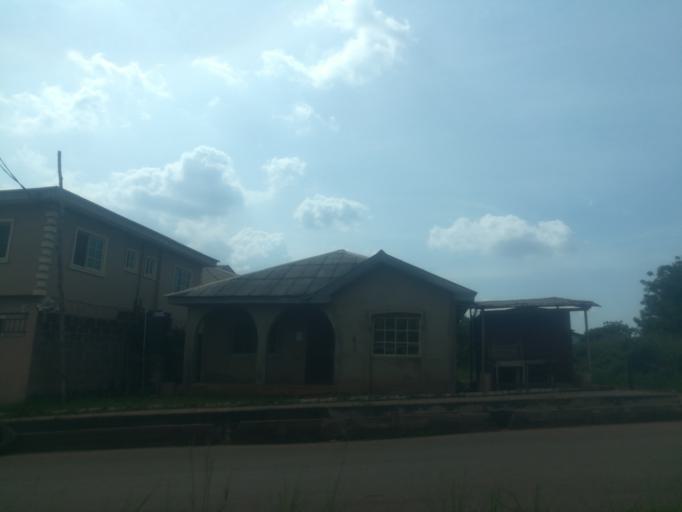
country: NG
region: Ogun
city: Abeokuta
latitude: 7.1729
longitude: 3.3833
